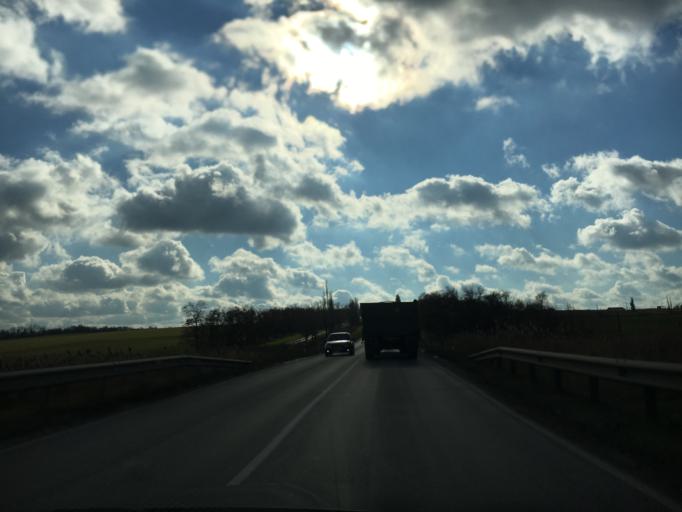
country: RU
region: Rostov
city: Matveyev Kurgan
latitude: 47.5482
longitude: 38.8907
